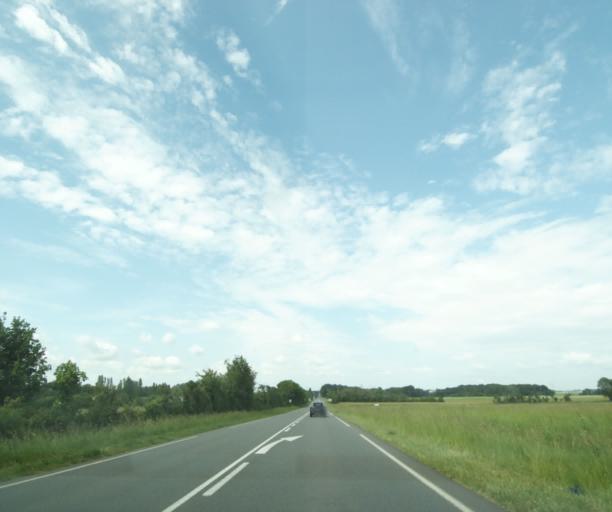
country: FR
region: Pays de la Loire
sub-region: Departement de Maine-et-Loire
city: Montreuil-Bellay
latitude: 47.1740
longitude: -0.1368
